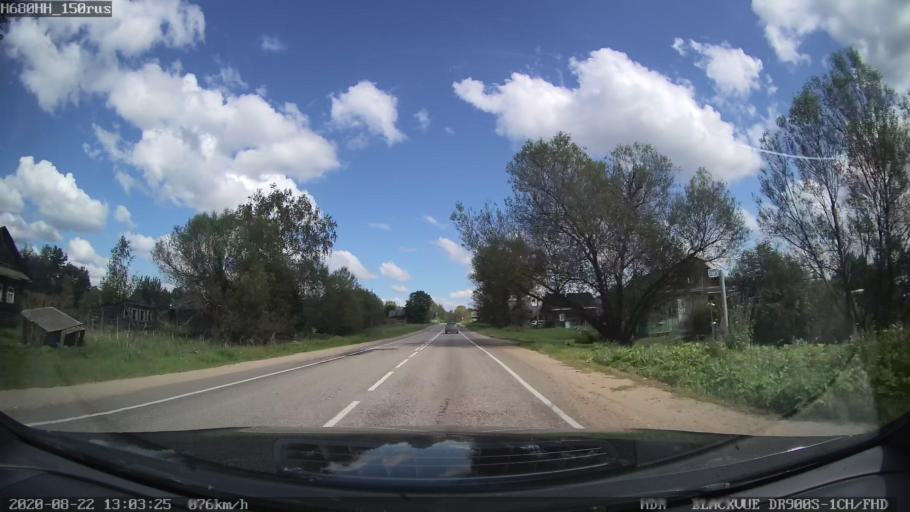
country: RU
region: Tverskaya
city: Bezhetsk
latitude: 57.6594
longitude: 36.4109
